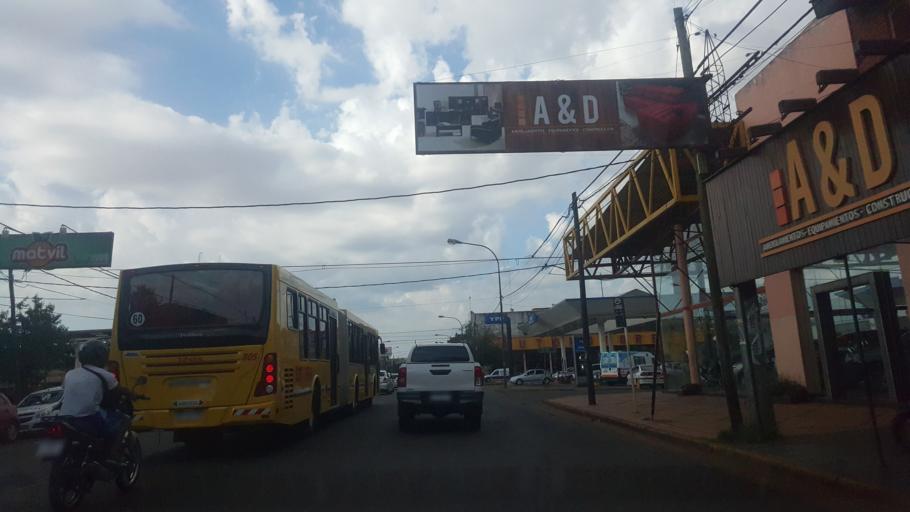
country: AR
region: Misiones
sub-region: Departamento de Capital
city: Posadas
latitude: -27.3919
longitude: -55.9009
